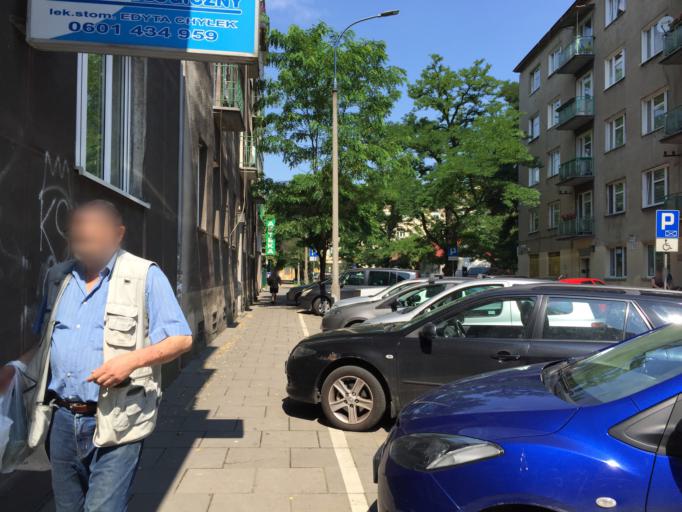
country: PL
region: Lesser Poland Voivodeship
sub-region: Krakow
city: Krakow
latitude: 50.0538
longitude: 19.9206
